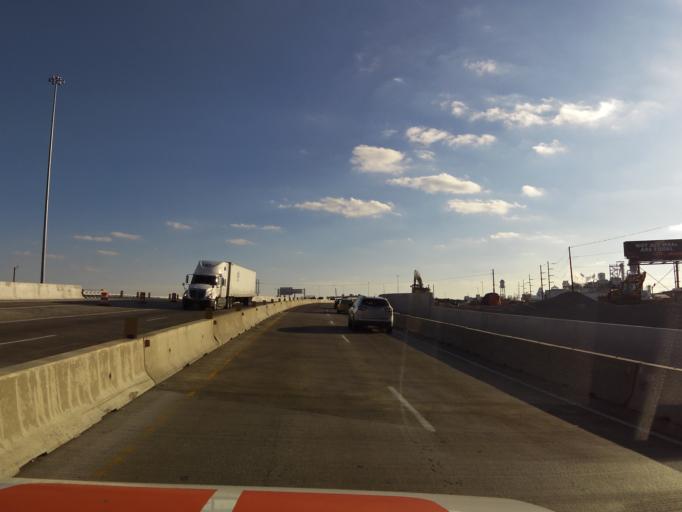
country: US
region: Indiana
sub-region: Clark County
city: Jeffersonville
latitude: 38.2798
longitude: -85.7500
